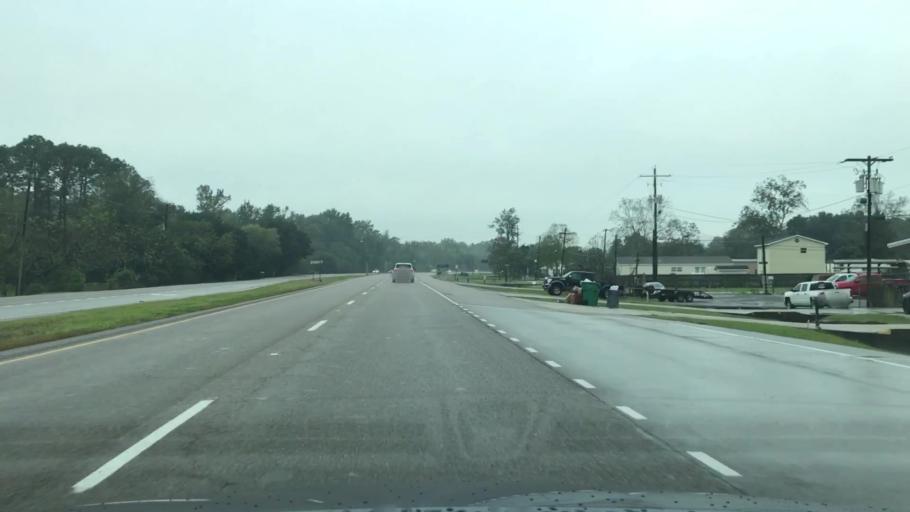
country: US
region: Louisiana
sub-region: Saint Charles Parish
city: Des Allemands
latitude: 29.8335
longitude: -90.4545
